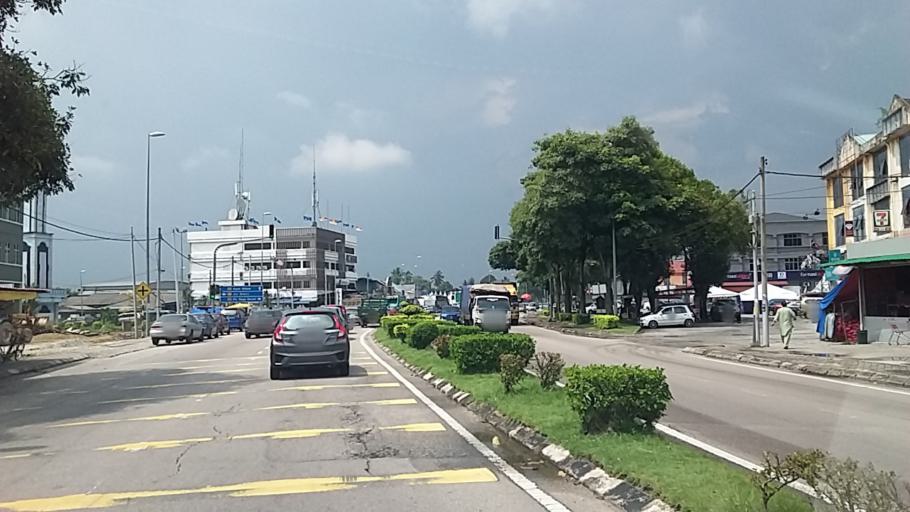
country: MY
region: Johor
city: Parit Raja
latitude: 1.8647
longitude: 103.1103
